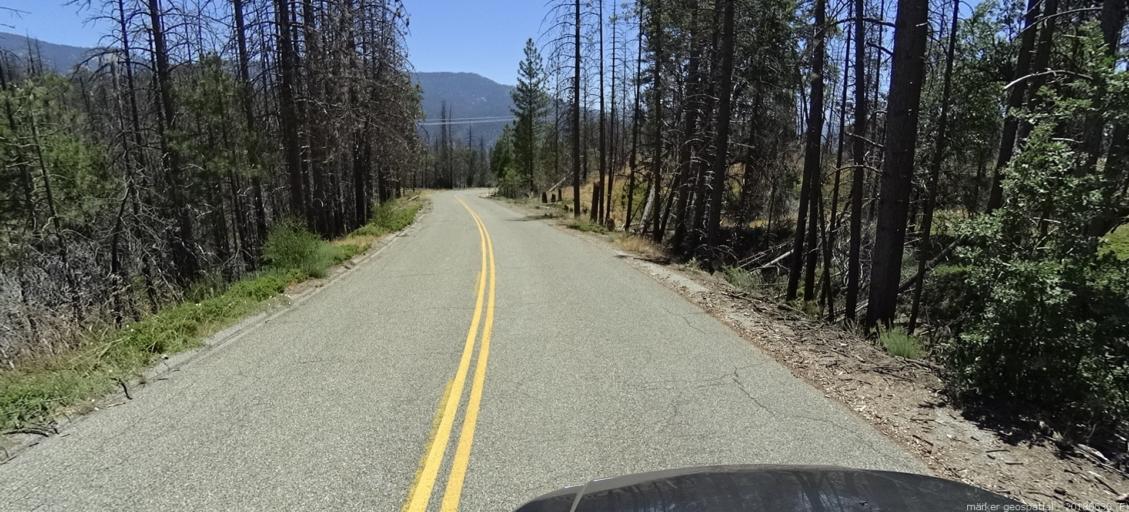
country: US
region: California
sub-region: Fresno County
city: Auberry
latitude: 37.2506
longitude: -119.3489
